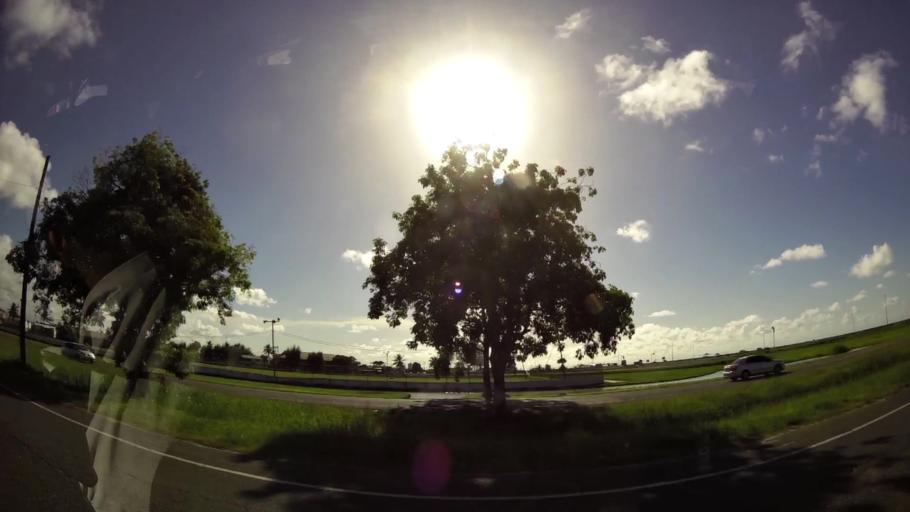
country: GY
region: Demerara-Mahaica
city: Georgetown
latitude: 6.8241
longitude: -58.1434
